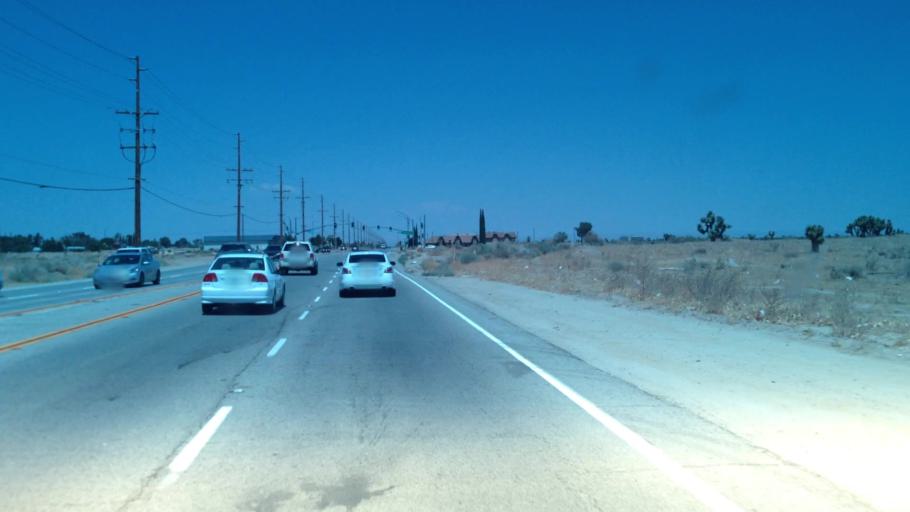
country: US
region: California
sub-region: Los Angeles County
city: Desert View Highlands
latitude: 34.6141
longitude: -118.1476
